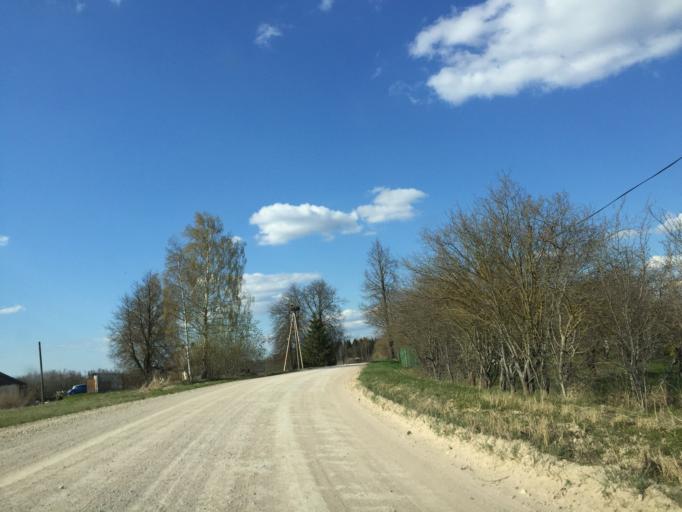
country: LV
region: Saulkrastu
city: Saulkrasti
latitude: 57.3472
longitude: 24.5788
